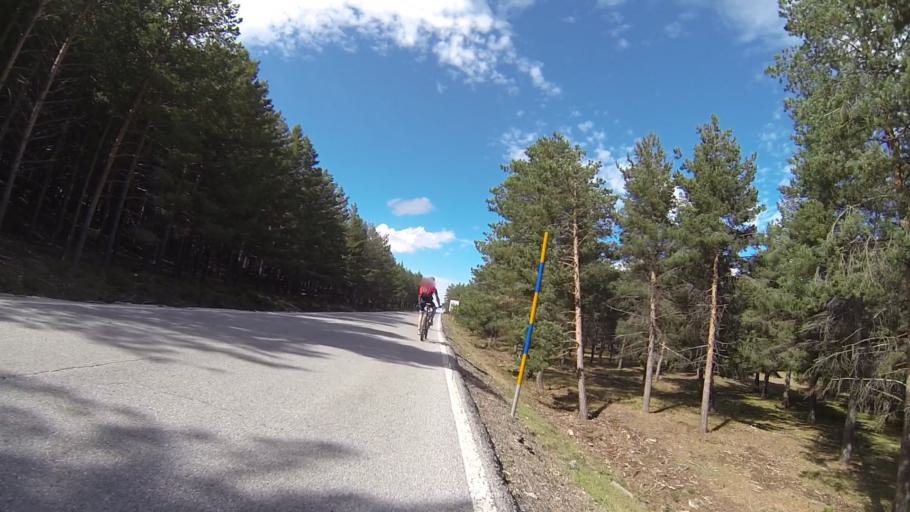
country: ES
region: Andalusia
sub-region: Provincia de Granada
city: Ferreira
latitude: 37.1115
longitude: -3.0291
